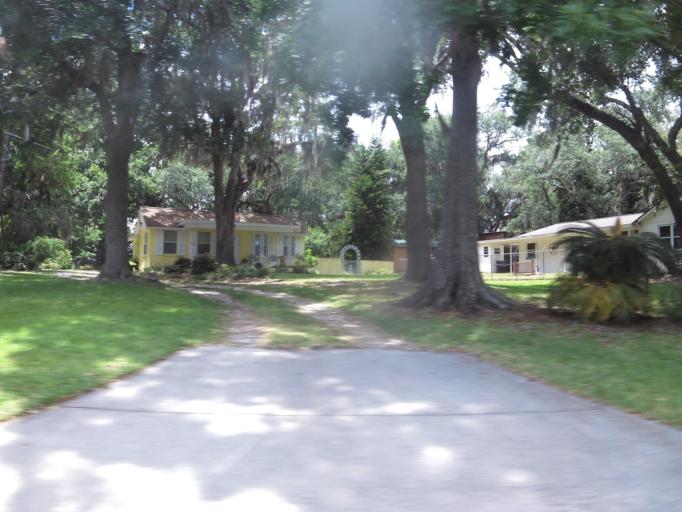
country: US
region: Florida
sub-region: Clay County
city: Orange Park
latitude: 30.1834
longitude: -81.6979
